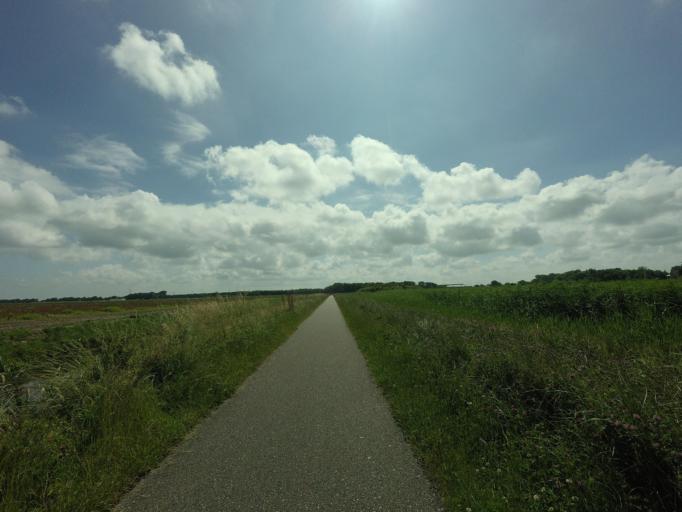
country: NL
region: North Holland
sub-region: Gemeente Schagen
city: Schagen
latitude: 52.8679
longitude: 4.8328
